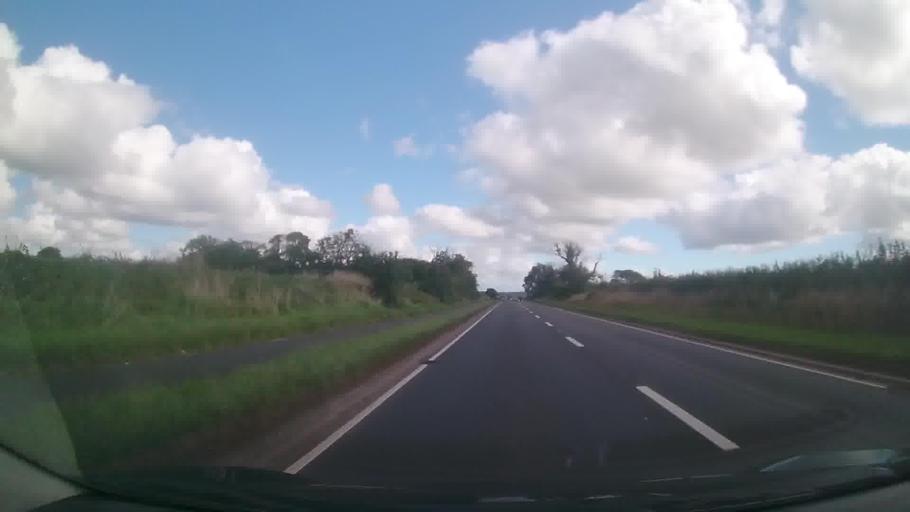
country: GB
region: Wales
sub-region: Pembrokeshire
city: Pembroke
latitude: 51.6901
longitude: -4.8505
